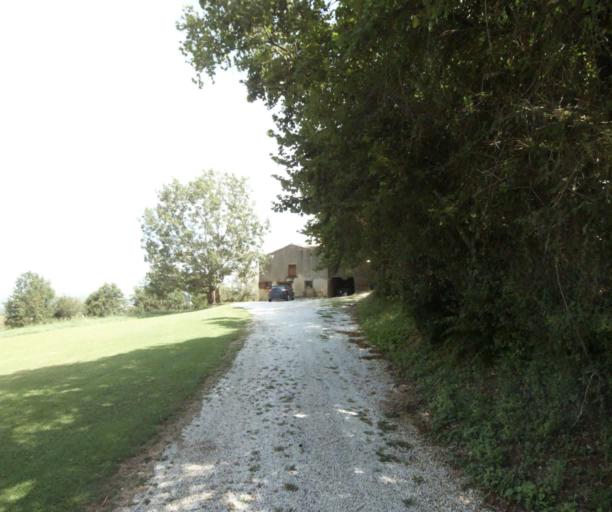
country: FR
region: Midi-Pyrenees
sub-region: Departement du Tarn
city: Soreze
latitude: 43.4588
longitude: 2.0966
